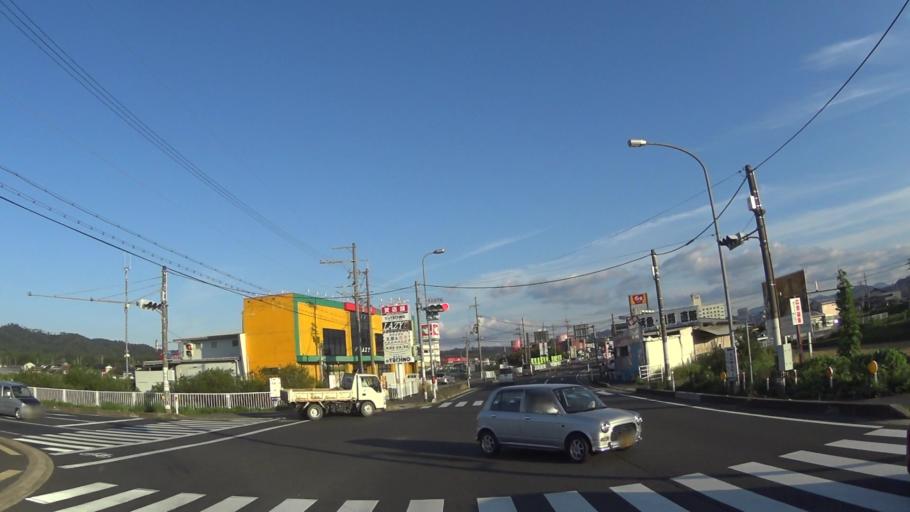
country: JP
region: Kyoto
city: Miyazu
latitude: 35.6097
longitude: 135.0792
